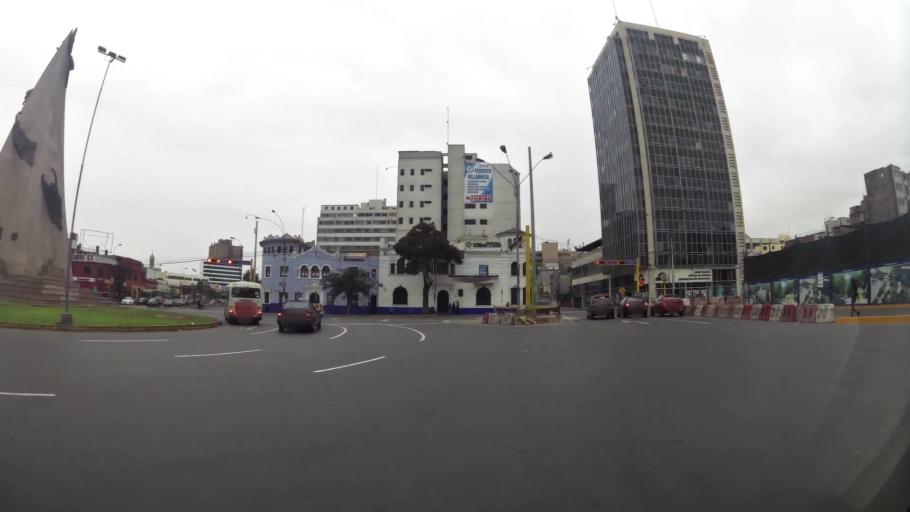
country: PE
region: Lima
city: Lima
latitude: -12.0648
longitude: -77.0390
